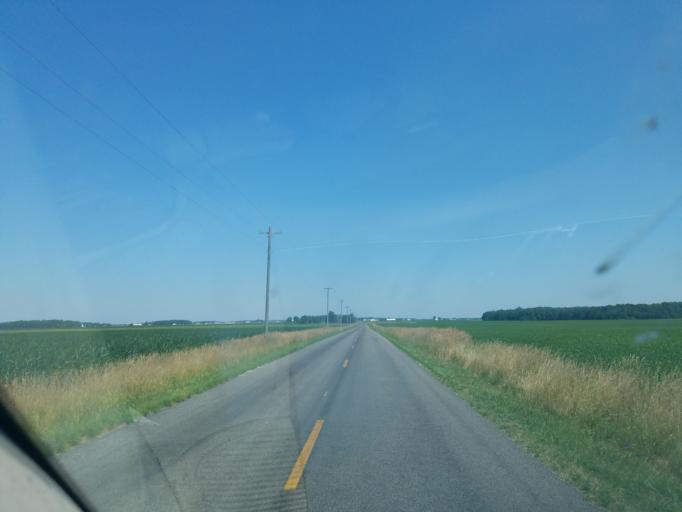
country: US
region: Ohio
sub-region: Mercer County
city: Rockford
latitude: 40.6348
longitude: -84.7087
